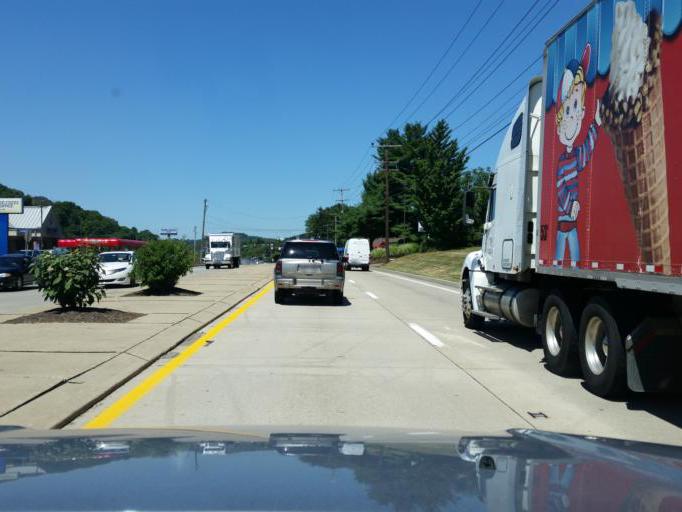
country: US
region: Pennsylvania
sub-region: Westmoreland County
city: Murrysville
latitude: 40.4235
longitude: -79.6643
